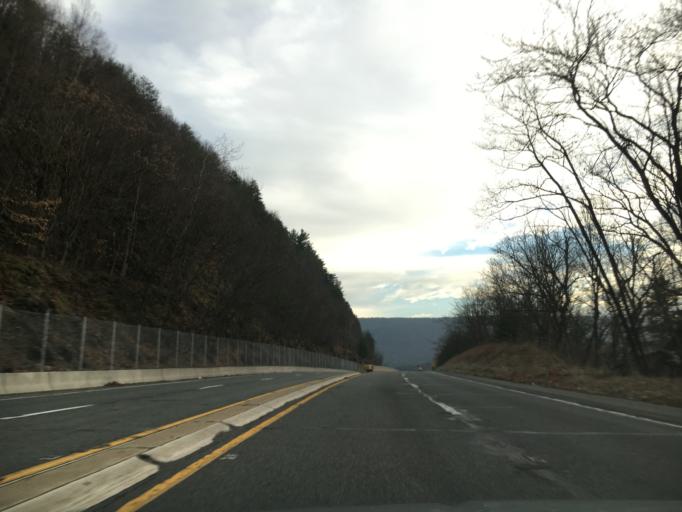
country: US
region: Pennsylvania
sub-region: Carbon County
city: Weissport East
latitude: 40.8104
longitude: -75.6692
